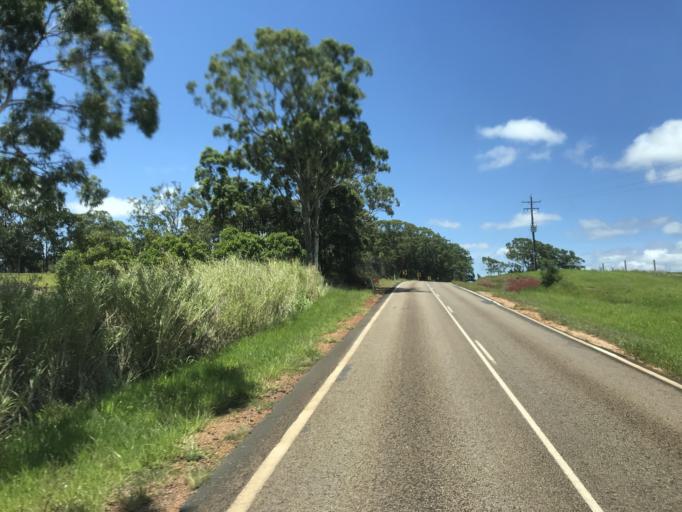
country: AU
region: Queensland
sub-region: Tablelands
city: Ravenshoe
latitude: -17.5160
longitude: 145.4506
